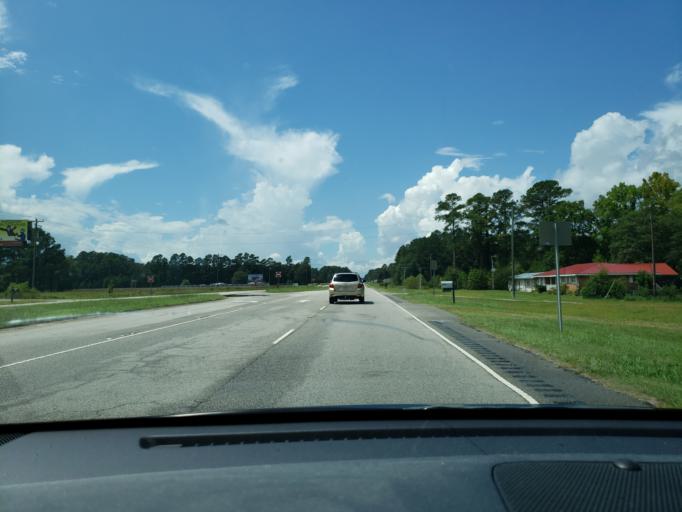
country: US
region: North Carolina
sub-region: Bladen County
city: Elizabethtown
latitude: 34.6455
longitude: -78.6937
